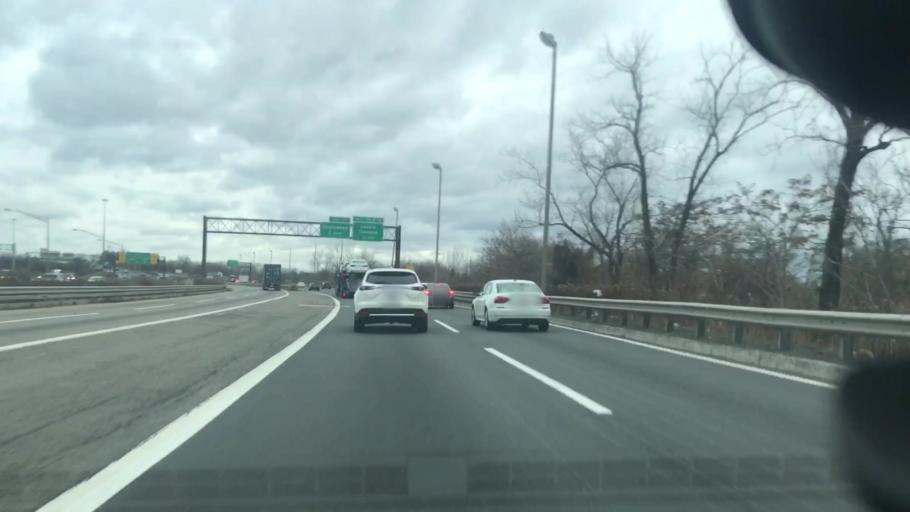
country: US
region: New Jersey
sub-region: Bergen County
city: Ridgefield Park
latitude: 40.8582
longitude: -74.0118
